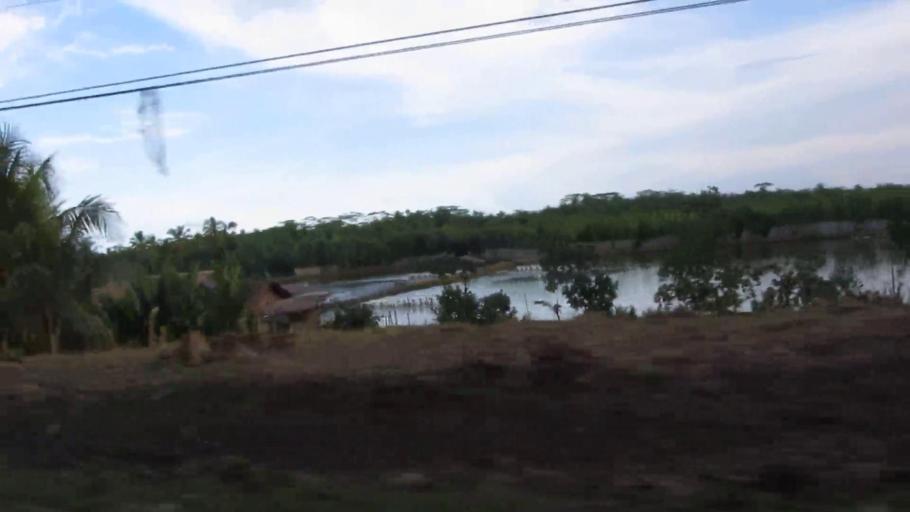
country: ID
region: West Java
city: Balengbeng
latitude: -7.7147
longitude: 108.4830
